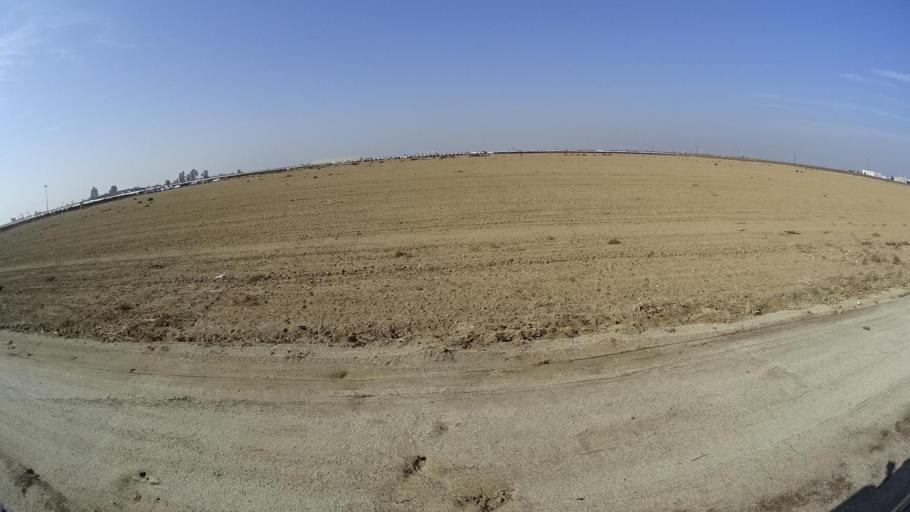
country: US
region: California
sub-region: Kern County
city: McFarland
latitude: 35.6940
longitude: -119.2231
